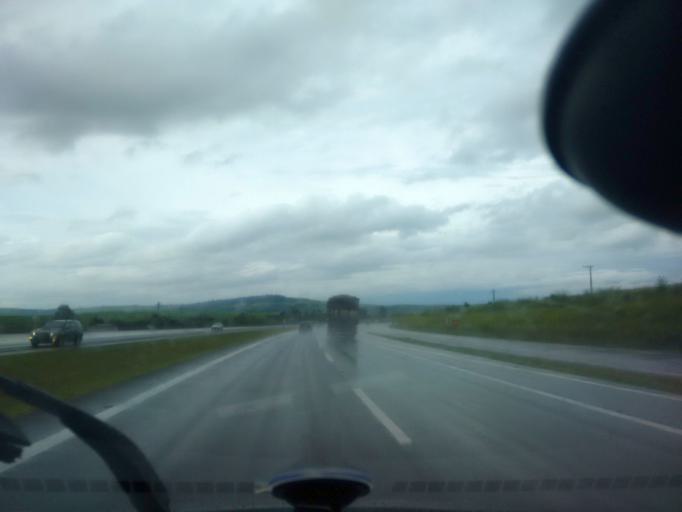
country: BR
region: Sao Paulo
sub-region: Iracemapolis
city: Iracemapolis
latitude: -22.5808
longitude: -47.4594
